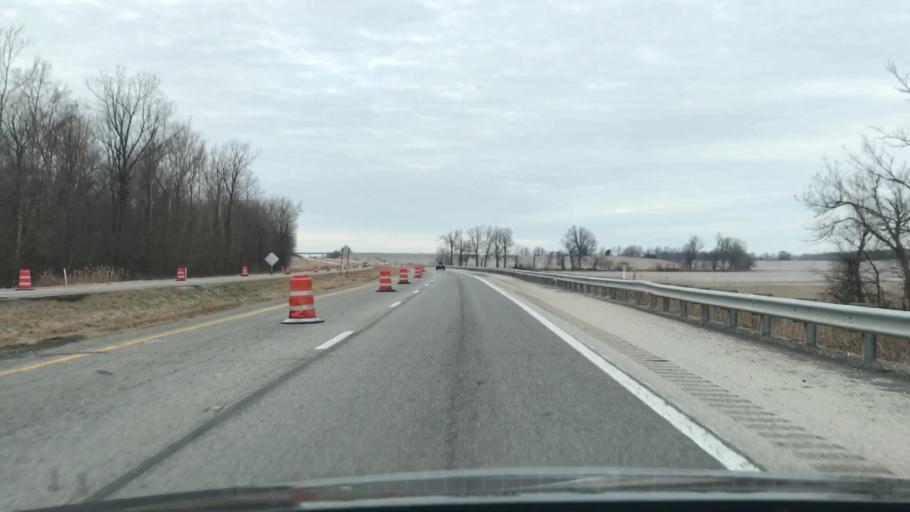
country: US
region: Kentucky
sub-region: Daviess County
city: Masonville
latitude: 37.6541
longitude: -87.0039
